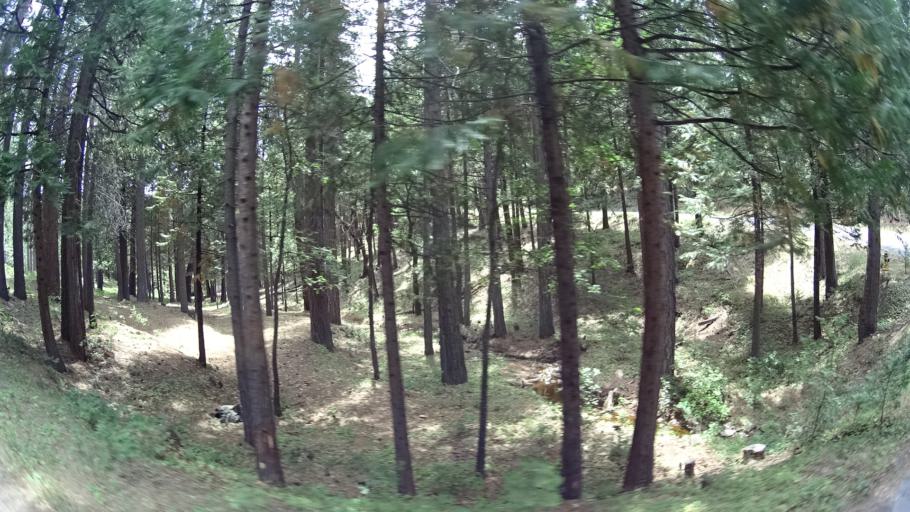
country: US
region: California
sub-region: Calaveras County
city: Arnold
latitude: 38.2390
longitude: -120.3447
